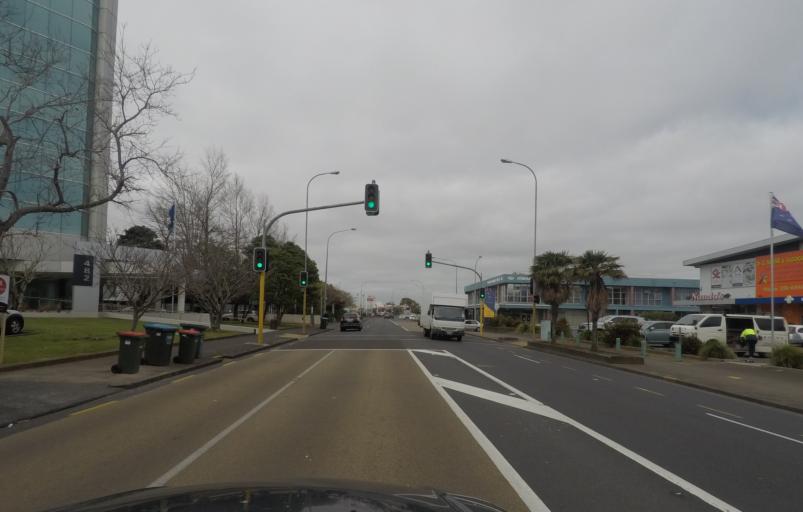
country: NZ
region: Auckland
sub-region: Auckland
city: Mangere
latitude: -36.9466
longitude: 174.8455
